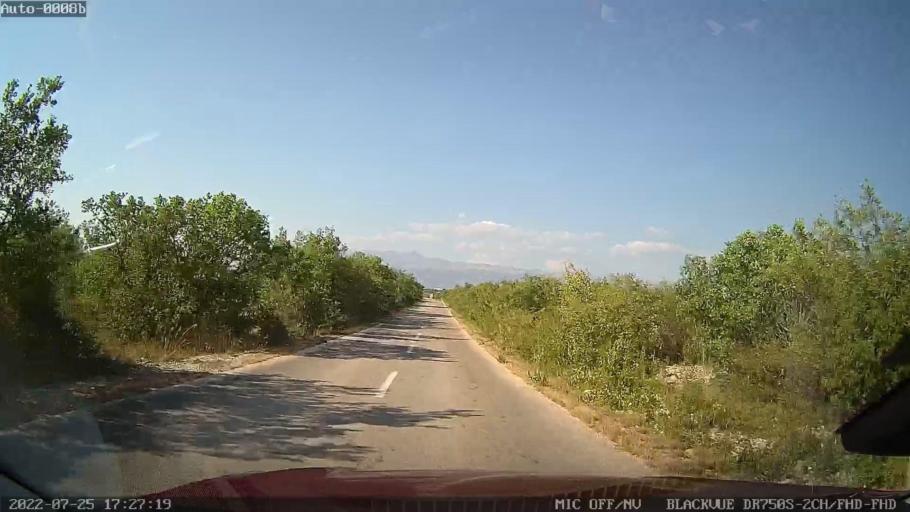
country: HR
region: Zadarska
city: Pridraga
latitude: 44.1420
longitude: 15.5043
